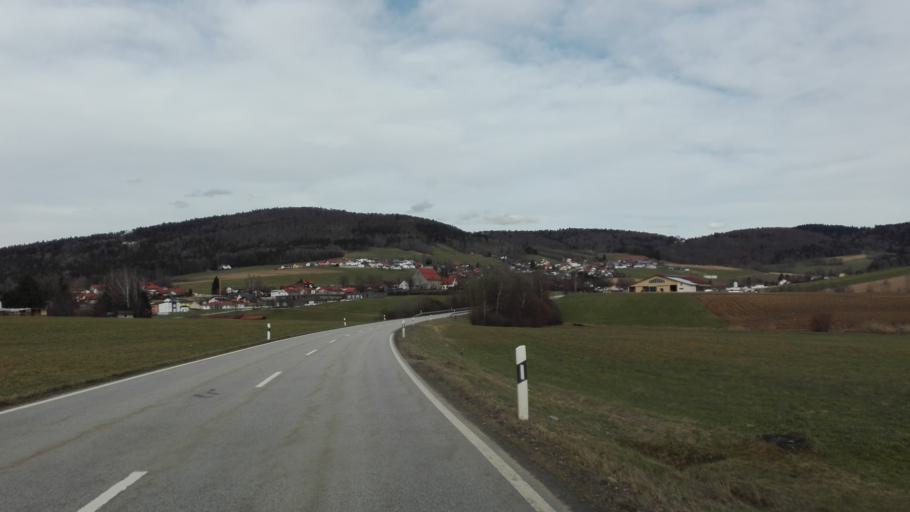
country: DE
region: Bavaria
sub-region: Lower Bavaria
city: Hauzenberg
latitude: 48.6310
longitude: 13.6577
